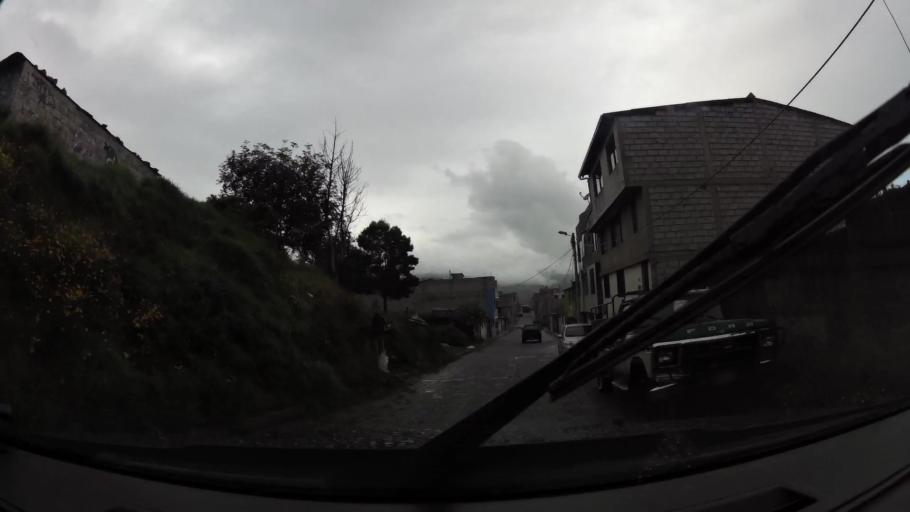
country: EC
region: Pichincha
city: Quito
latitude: -0.0974
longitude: -78.5131
